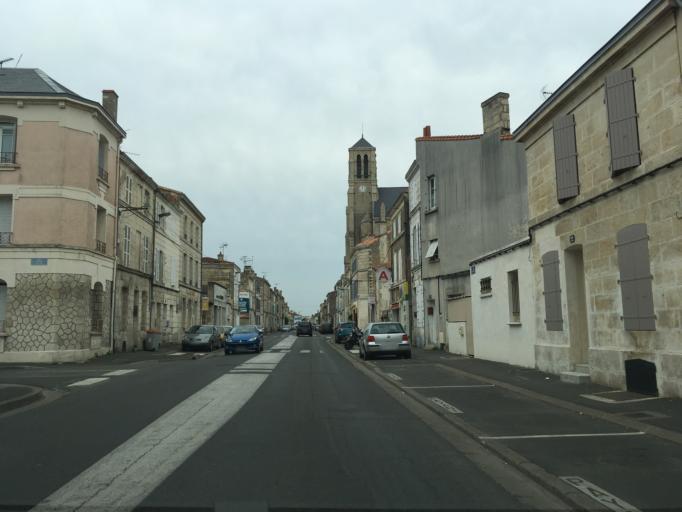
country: FR
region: Poitou-Charentes
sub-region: Departement des Deux-Sevres
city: Niort
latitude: 46.3265
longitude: -0.4687
